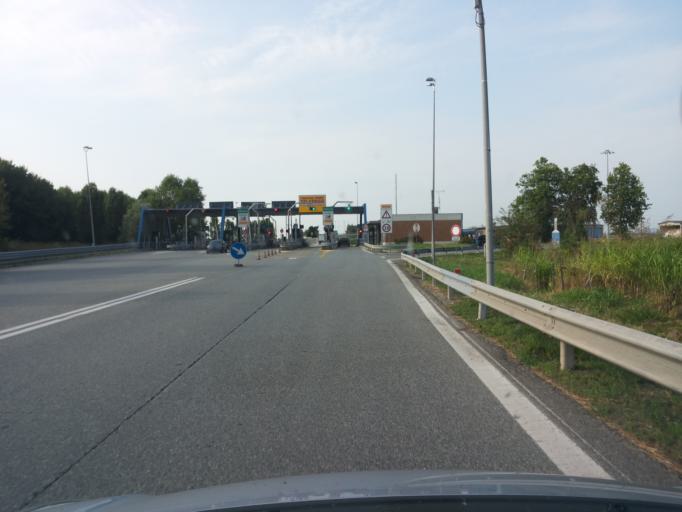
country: IT
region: Piedmont
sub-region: Provincia di Vercelli
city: Asigliano Vercellese
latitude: 45.2953
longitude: 8.3888
